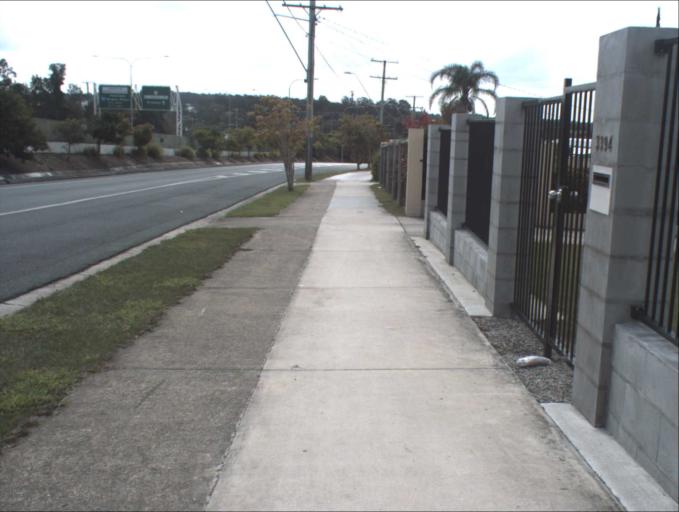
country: AU
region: Queensland
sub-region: Logan
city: Park Ridge South
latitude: -27.6686
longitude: 153.0332
